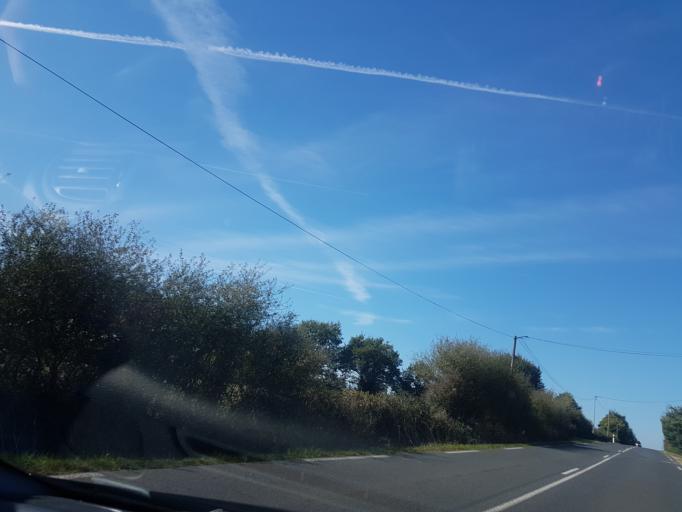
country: FR
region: Pays de la Loire
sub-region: Departement de la Loire-Atlantique
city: Casson
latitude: 47.4281
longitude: -1.5817
